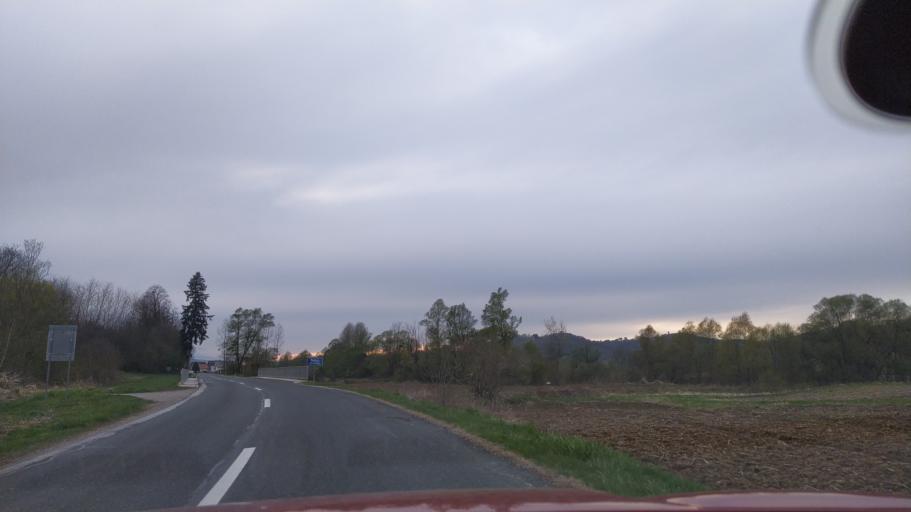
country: HR
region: Varazdinska
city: Jalzabet
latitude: 46.2183
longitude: 16.5234
